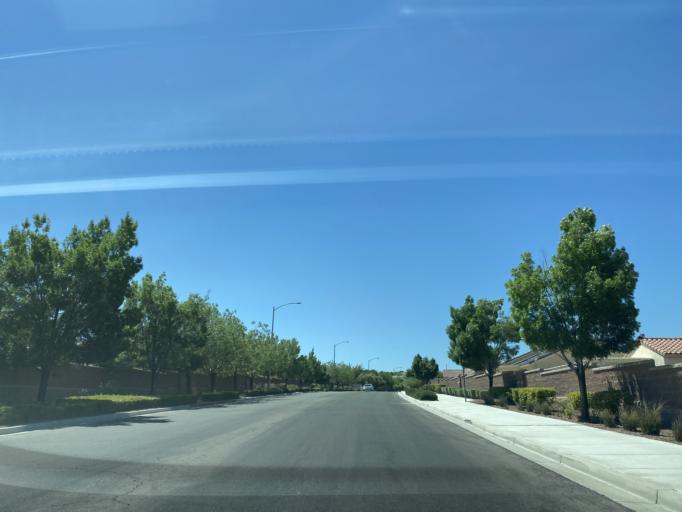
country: US
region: Nevada
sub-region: Clark County
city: Whitney
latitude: 35.9520
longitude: -115.0851
